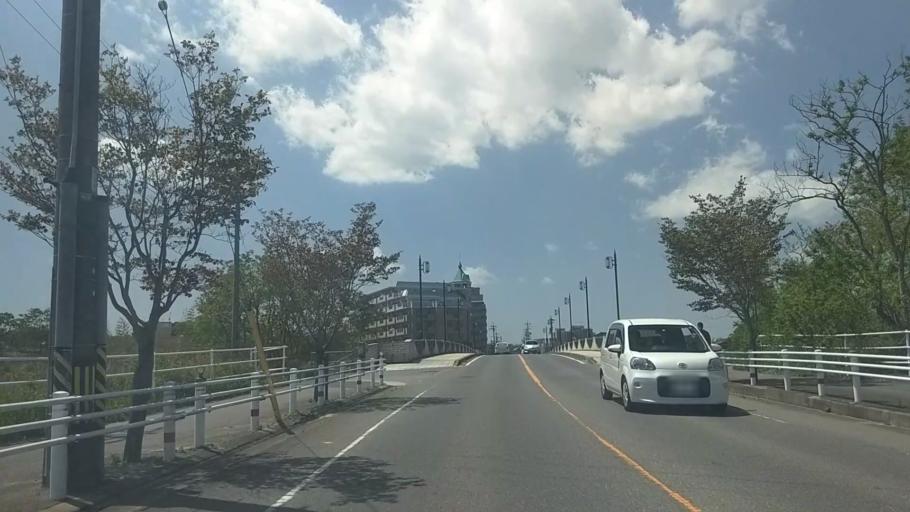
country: JP
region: Aichi
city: Okazaki
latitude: 34.9398
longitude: 137.1873
